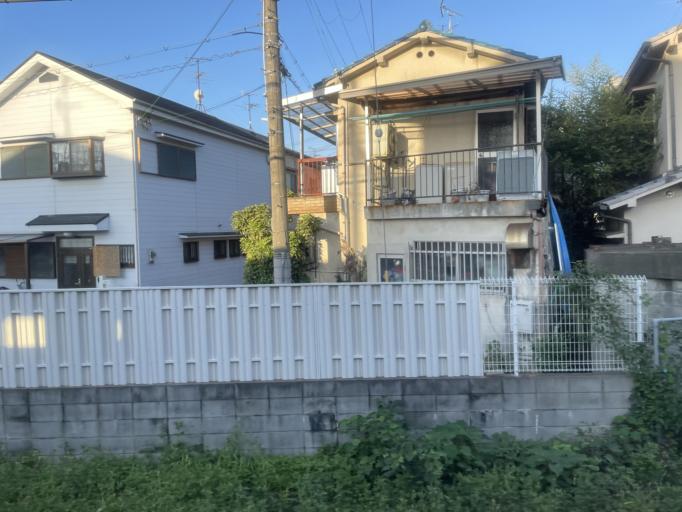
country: JP
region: Osaka
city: Matsubara
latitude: 34.5801
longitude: 135.5383
